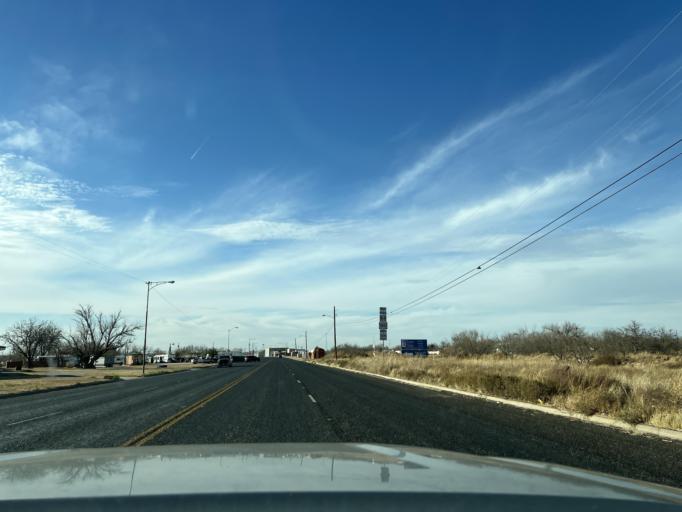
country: US
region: Texas
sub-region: Scurry County
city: Snyder
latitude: 32.7129
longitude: -100.8939
